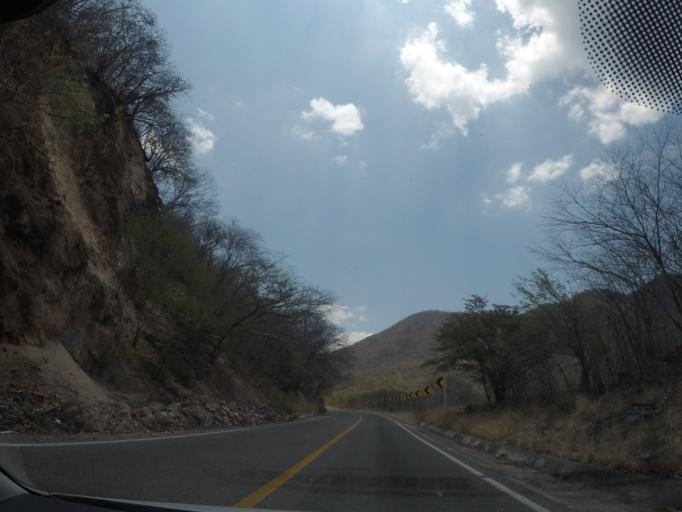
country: MX
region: Oaxaca
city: Santa Maria Jalapa del Marques
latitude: 16.4023
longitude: -95.4092
